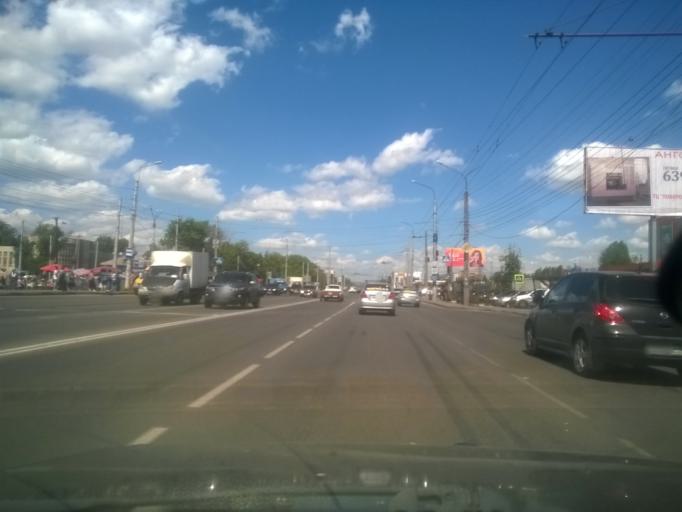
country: RU
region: Kursk
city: Kursk
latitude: 51.6616
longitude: 36.1368
